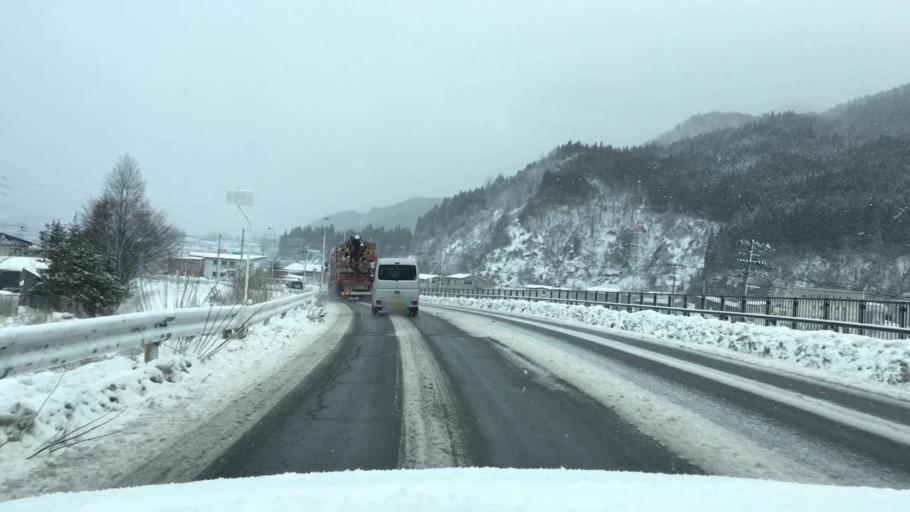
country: JP
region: Aomori
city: Kuroishi
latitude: 40.5216
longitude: 140.5827
